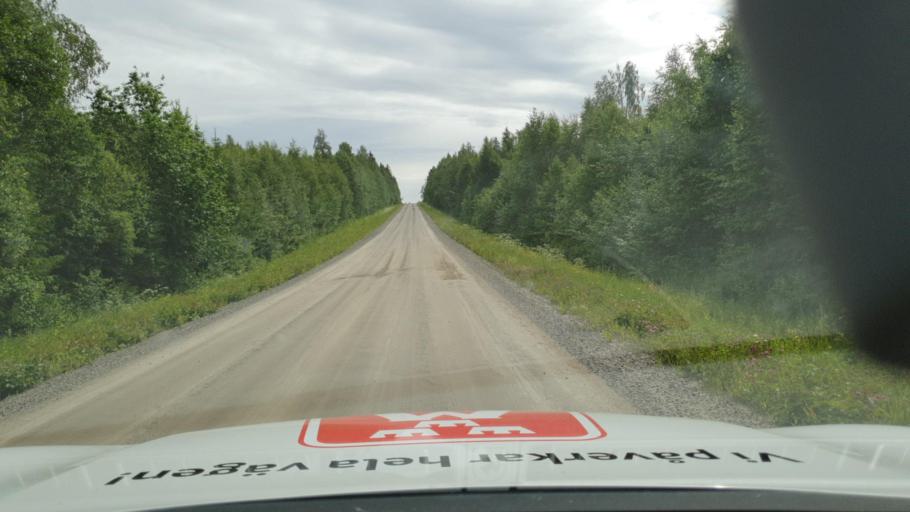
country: SE
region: Vaesterbotten
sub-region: Skelleftea Kommun
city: Burtraesk
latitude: 64.3931
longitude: 20.4114
